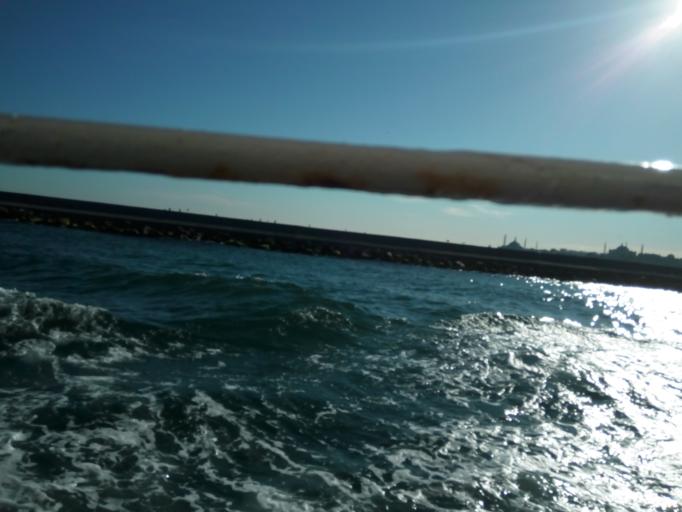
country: TR
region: Istanbul
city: UEskuedar
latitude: 41.0069
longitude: 29.0042
